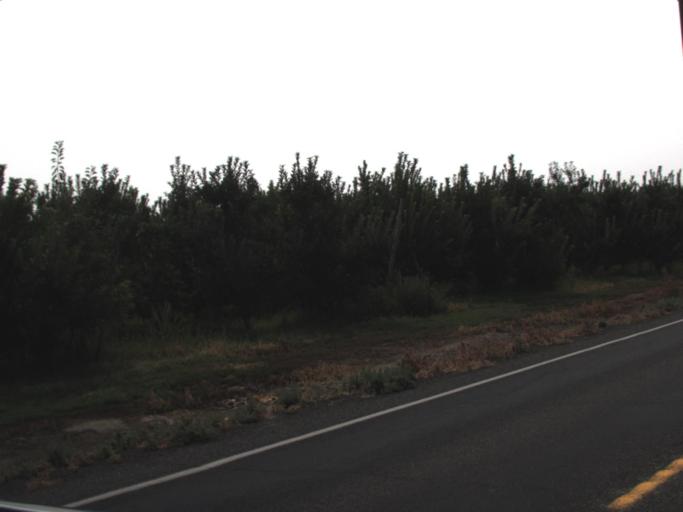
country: US
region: Washington
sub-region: Yakima County
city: Sunnyside
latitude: 46.3699
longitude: -119.9756
